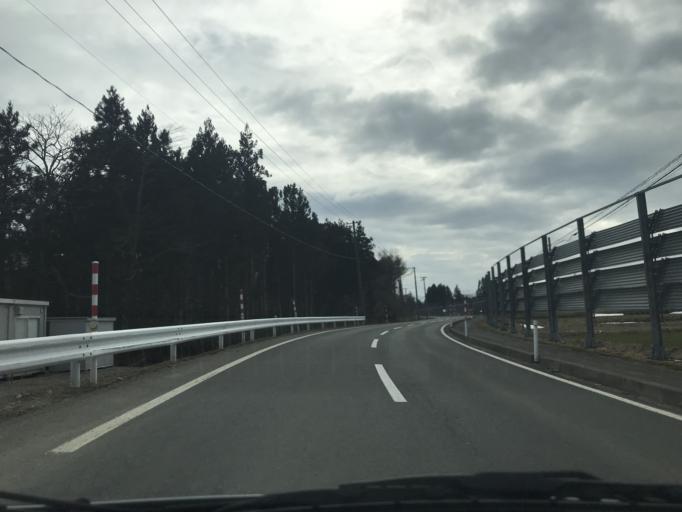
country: JP
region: Iwate
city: Hanamaki
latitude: 39.3769
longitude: 141.0071
